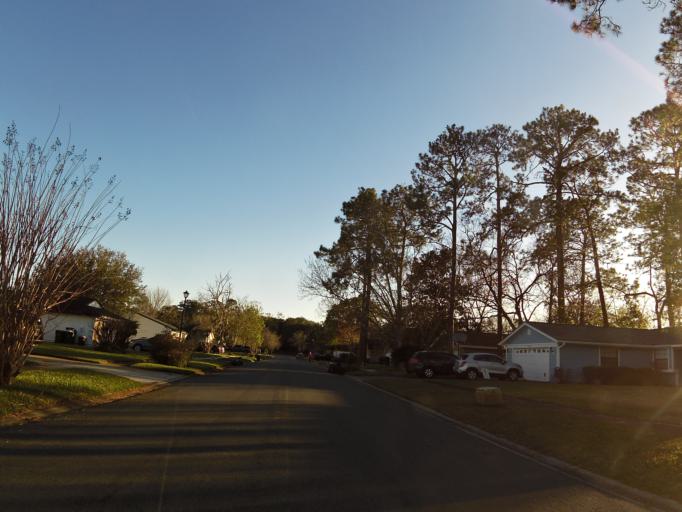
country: US
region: Florida
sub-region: Saint Johns County
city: Fruit Cove
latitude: 30.1746
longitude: -81.5833
